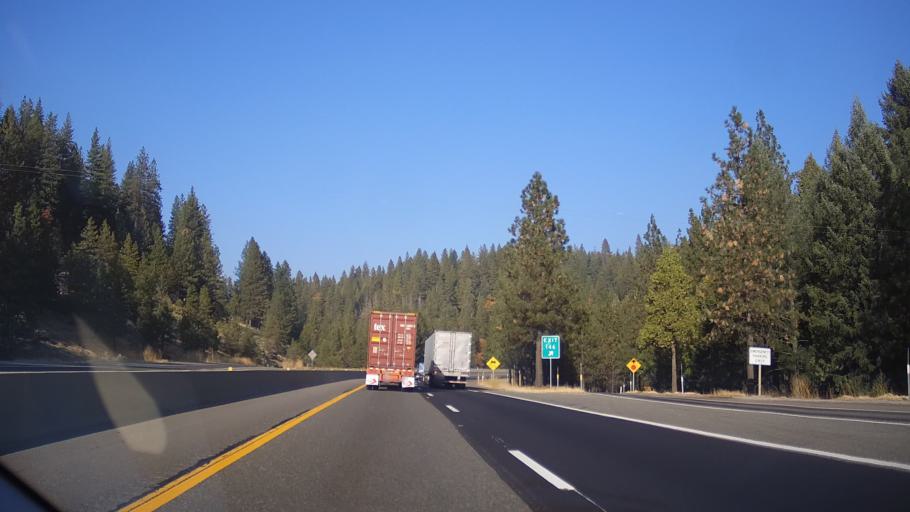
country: US
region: California
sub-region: Placer County
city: Colfax
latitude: 39.1996
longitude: -120.8138
